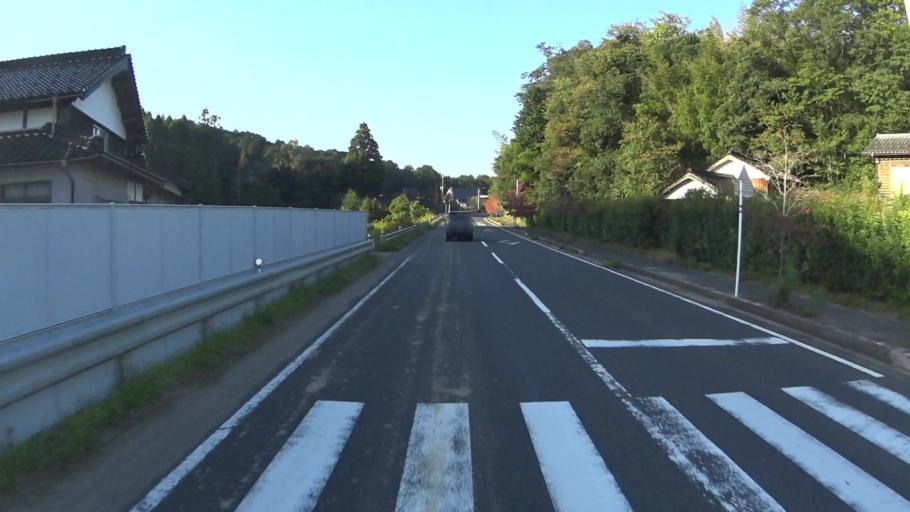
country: JP
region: Hyogo
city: Toyooka
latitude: 35.6100
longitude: 134.9195
